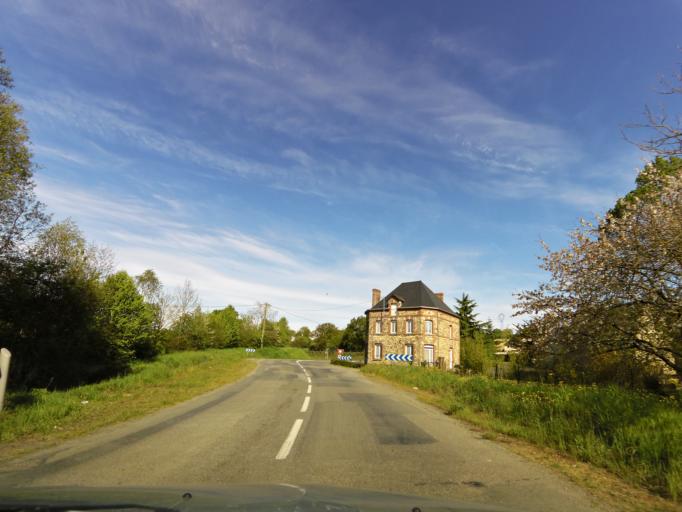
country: FR
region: Brittany
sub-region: Departement d'Ille-et-Vilaine
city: Pance
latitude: 47.8744
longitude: -1.6463
